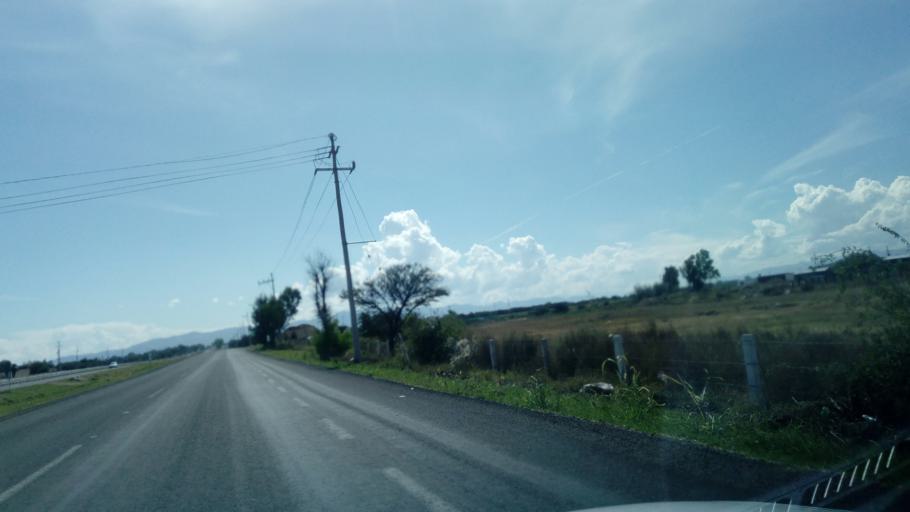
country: MX
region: Durango
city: Victoria de Durango
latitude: 24.0814
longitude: -104.5565
